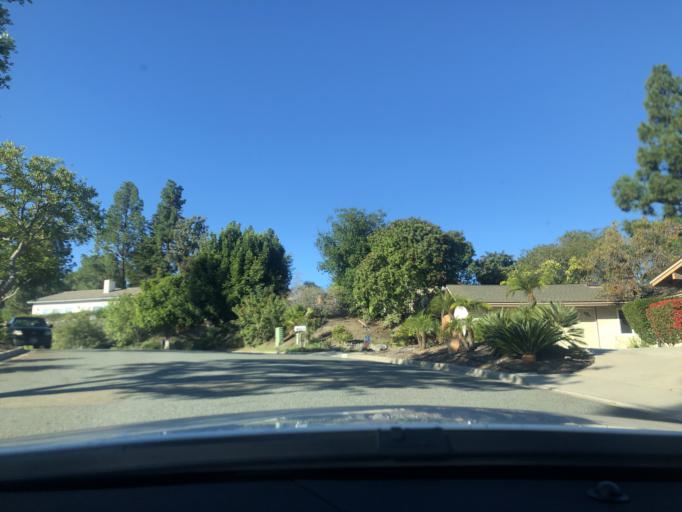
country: US
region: California
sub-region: San Diego County
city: Casa de Oro-Mount Helix
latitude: 32.7686
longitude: -116.9594
